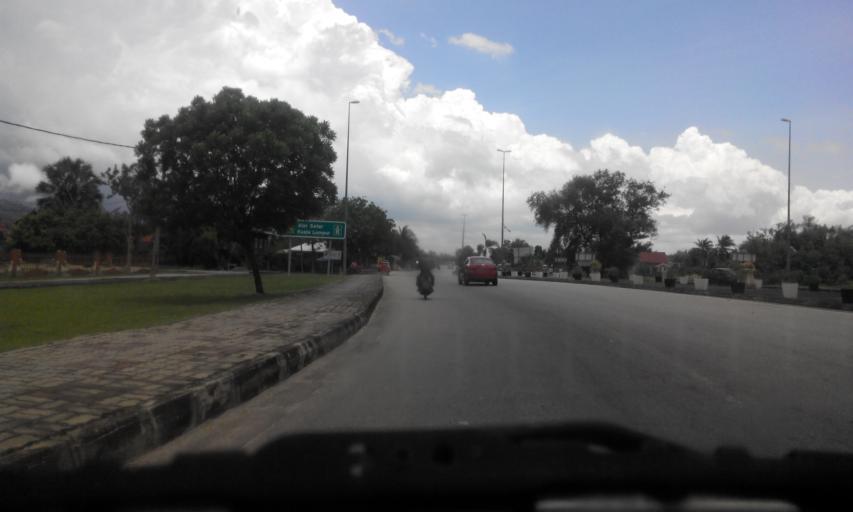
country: MY
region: Perak
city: Parit Buntar
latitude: 5.1314
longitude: 100.4977
